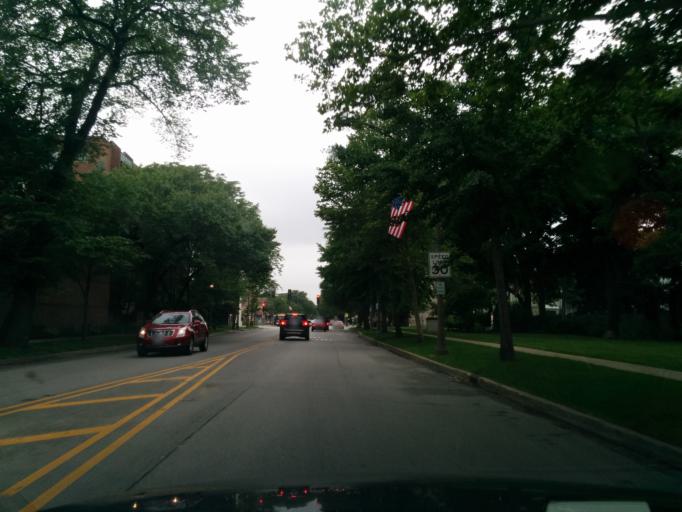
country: US
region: Illinois
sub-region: Cook County
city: Forest Park
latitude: 41.8884
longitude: -87.8131
